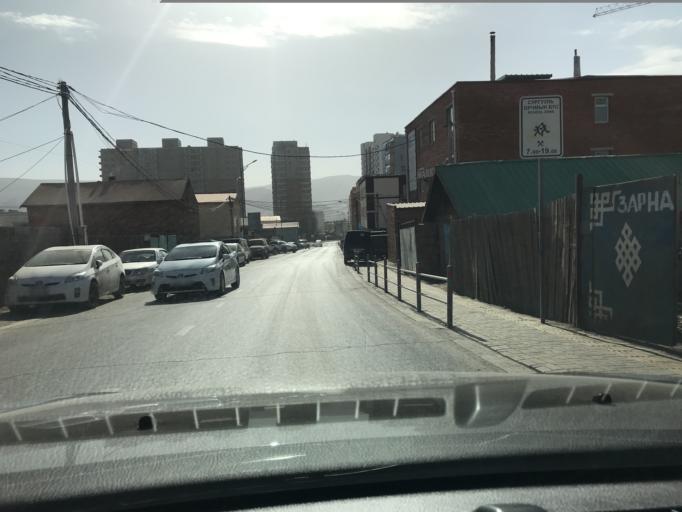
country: MN
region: Ulaanbaatar
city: Ulaanbaatar
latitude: 47.9230
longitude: 106.9611
